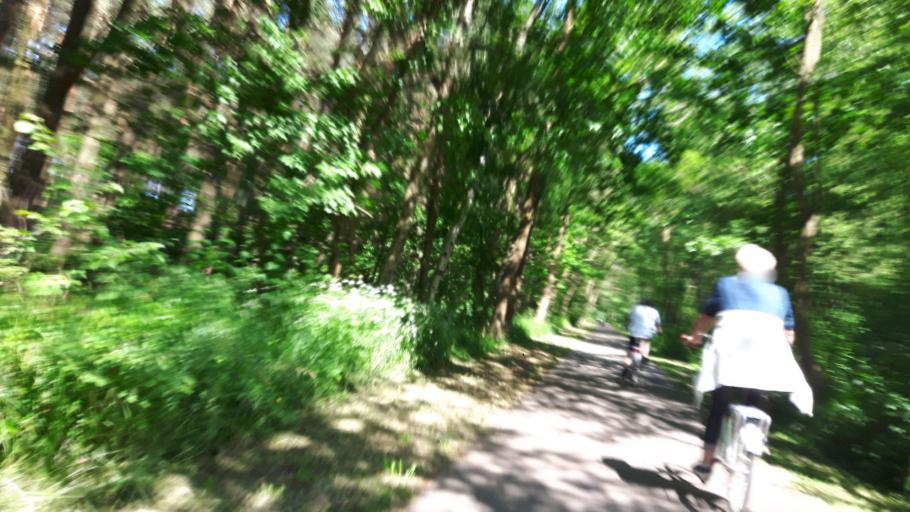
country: PL
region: West Pomeranian Voivodeship
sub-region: Powiat kolobrzeski
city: Grzybowo
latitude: 54.1646
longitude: 15.4777
